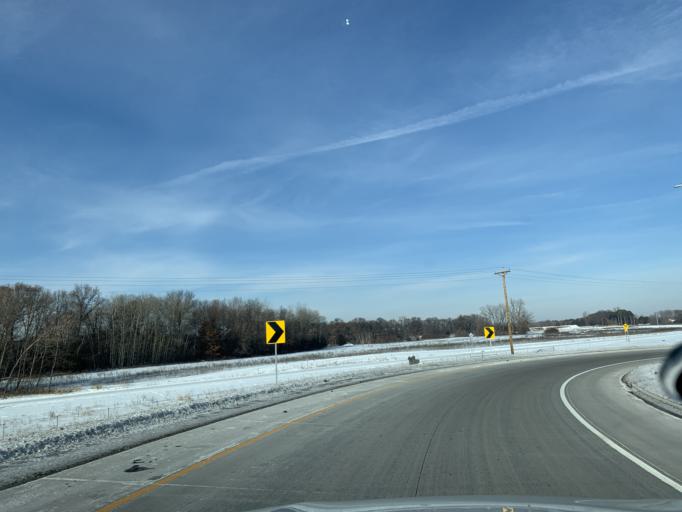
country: US
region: Minnesota
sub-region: Washington County
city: Forest Lake
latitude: 45.2905
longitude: -93.0048
